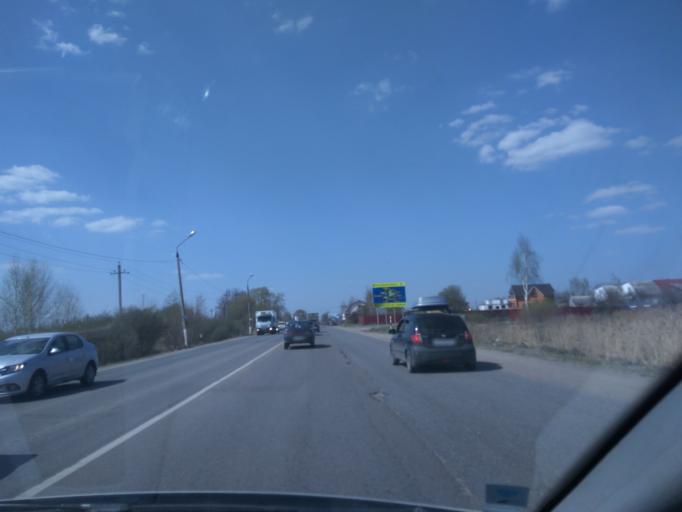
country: RU
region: Moskovskaya
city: Ramenskoye
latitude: 55.5478
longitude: 38.2835
